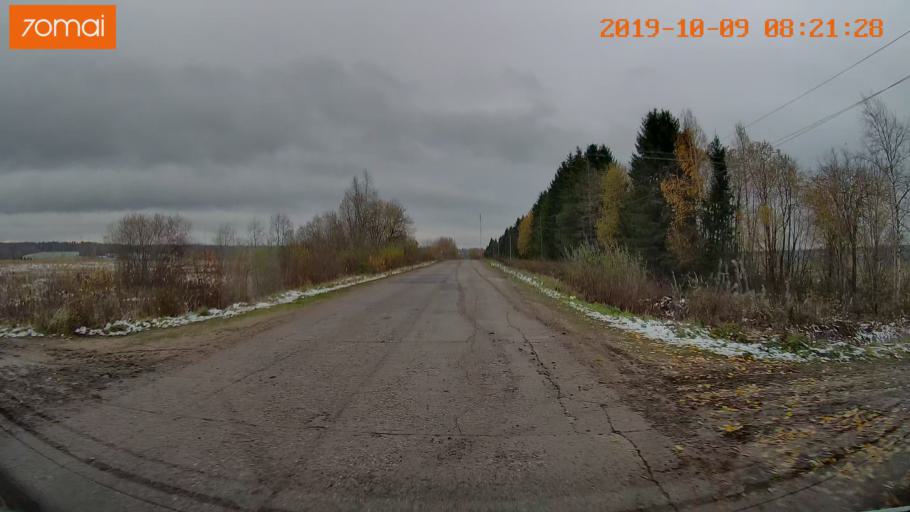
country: RU
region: Vologda
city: Gryazovets
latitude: 58.7421
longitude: 40.2775
